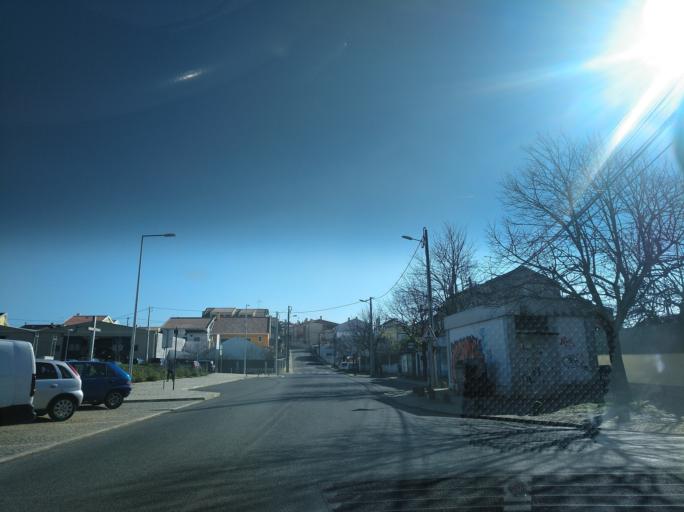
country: PT
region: Lisbon
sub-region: Odivelas
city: Canecas
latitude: 38.8067
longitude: -9.2198
